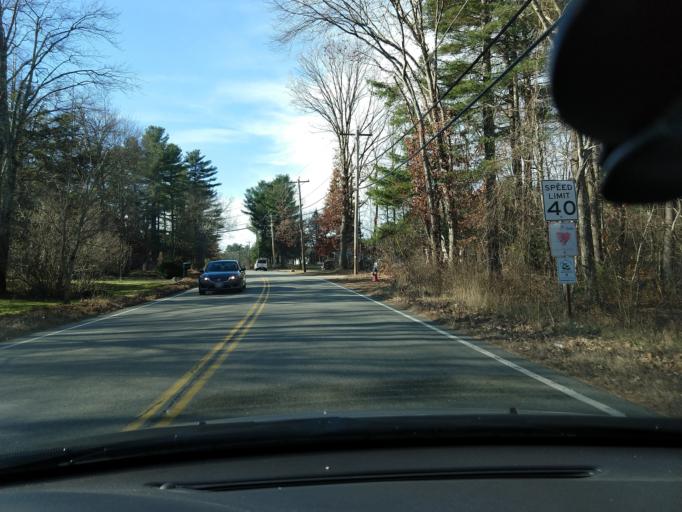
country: US
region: Massachusetts
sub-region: Middlesex County
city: East Pepperell
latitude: 42.6690
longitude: -71.5330
